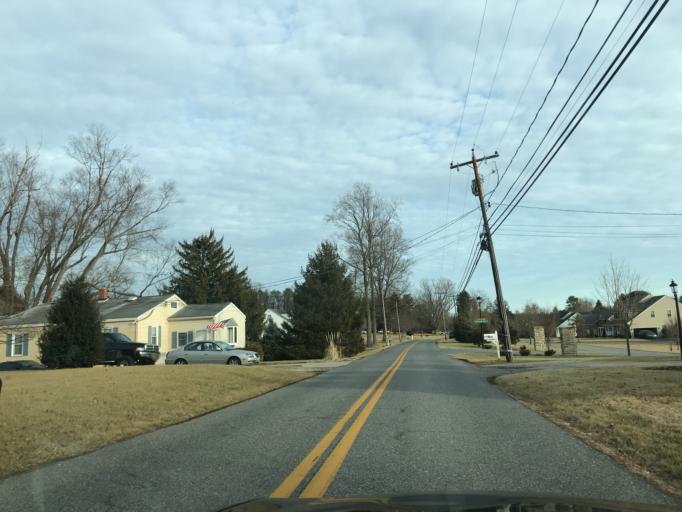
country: US
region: Maryland
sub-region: Baltimore County
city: Kingsville
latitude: 39.4509
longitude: -76.4070
